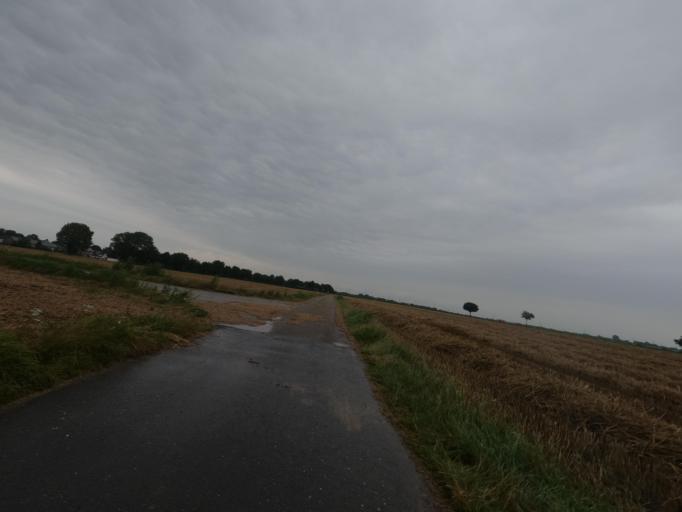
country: DE
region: North Rhine-Westphalia
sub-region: Regierungsbezirk Koln
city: Ubach-Palenberg
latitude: 50.9397
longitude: 6.1559
